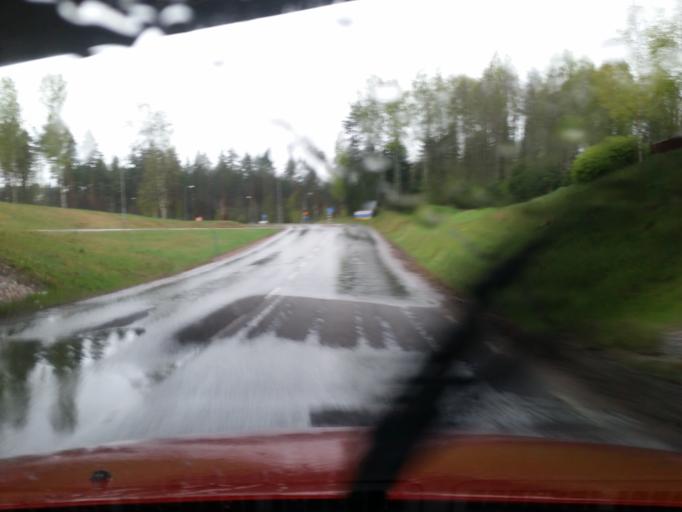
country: SE
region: Dalarna
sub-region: Leksand Municipality
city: Smedby
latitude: 60.6755
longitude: 15.0867
